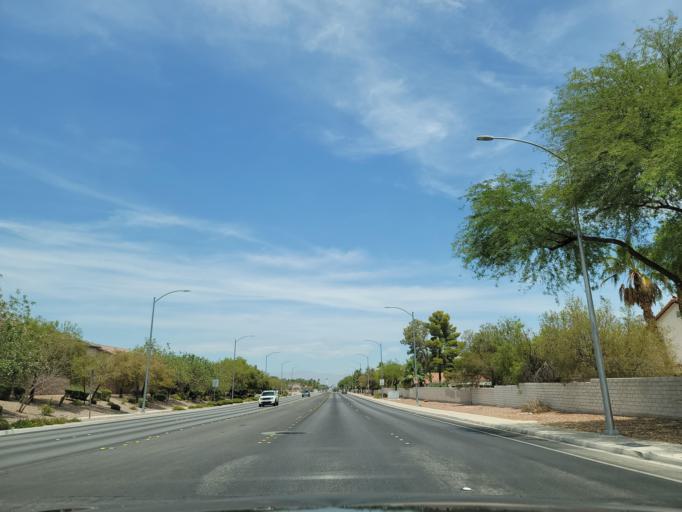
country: US
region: Nevada
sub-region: Clark County
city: Paradise
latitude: 36.0350
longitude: -115.1544
